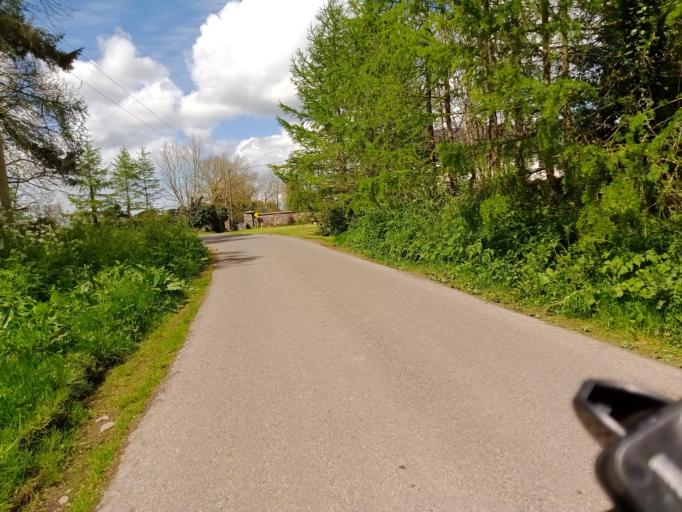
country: IE
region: Leinster
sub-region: Kilkenny
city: Thomastown
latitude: 52.5860
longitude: -7.1404
